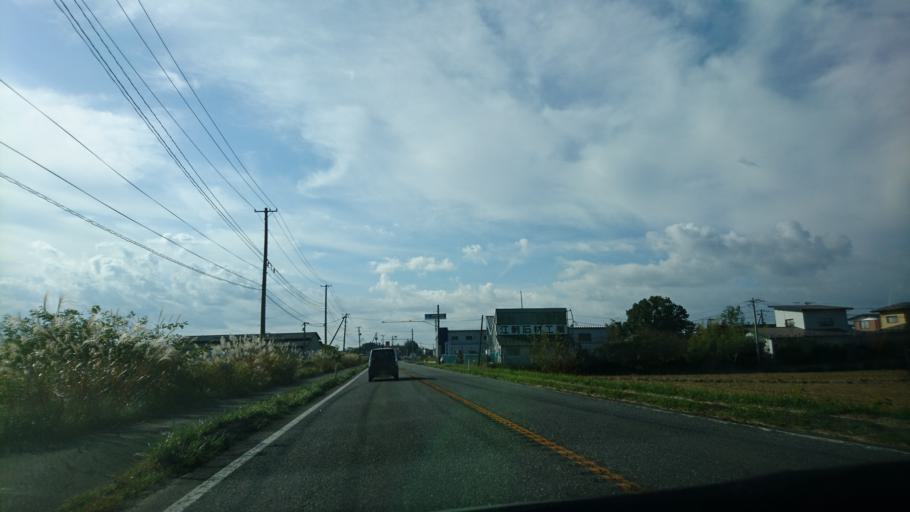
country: JP
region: Miyagi
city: Furukawa
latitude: 38.6107
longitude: 140.9831
